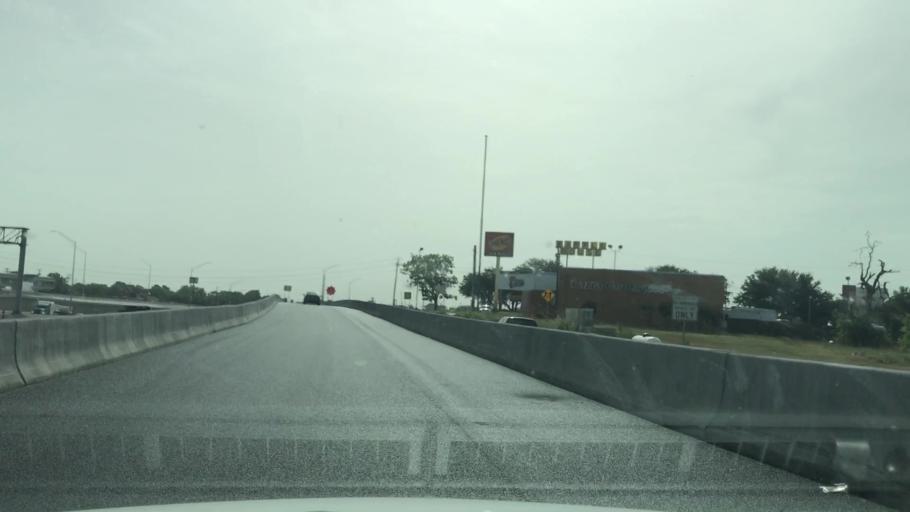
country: US
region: Texas
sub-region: Tarrant County
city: Euless
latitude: 32.8378
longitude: -97.0869
